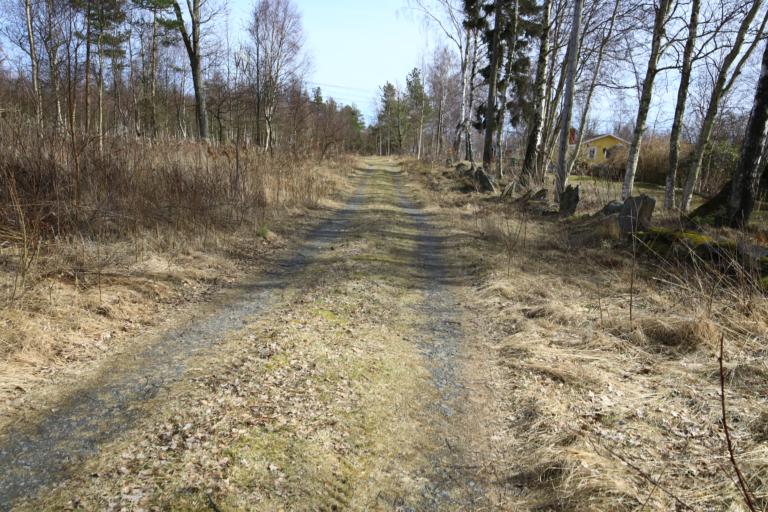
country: SE
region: Halland
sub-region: Kungsbacka Kommun
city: Frillesas
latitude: 57.2685
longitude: 12.1218
